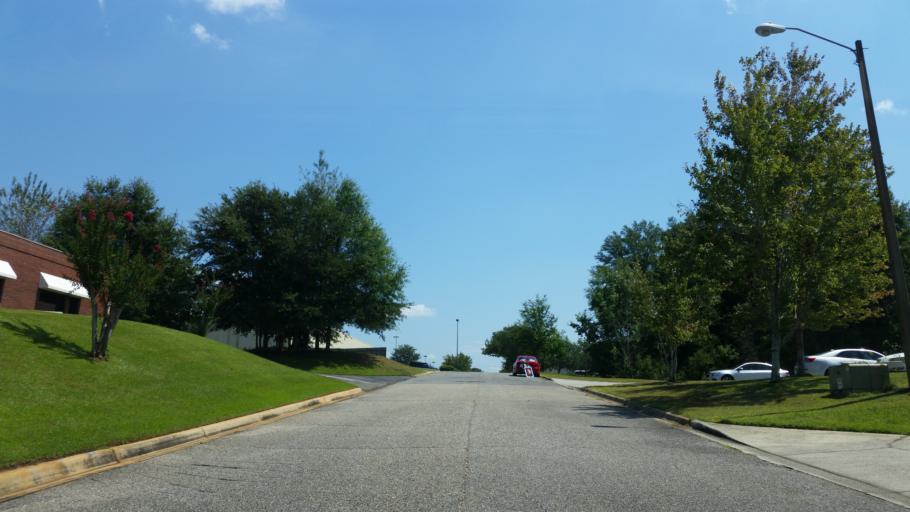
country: US
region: Florida
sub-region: Escambia County
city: Brent
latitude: 30.4893
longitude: -87.2276
